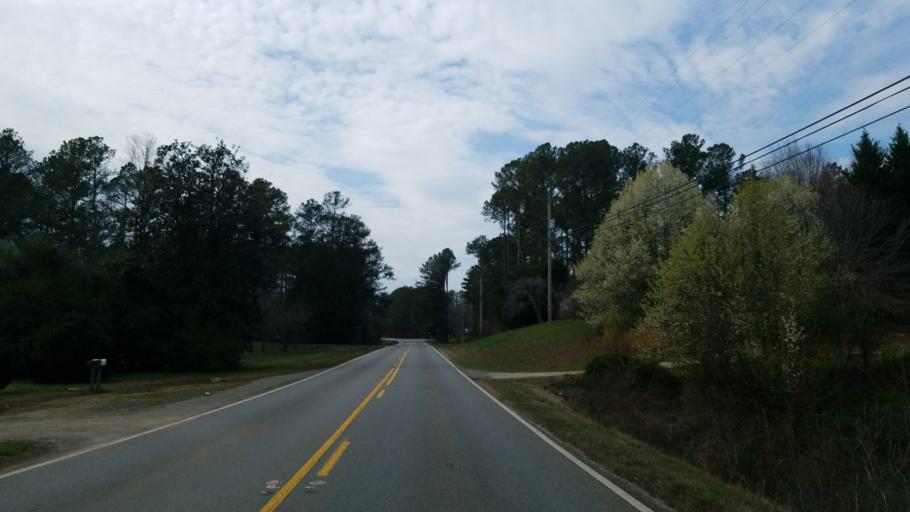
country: US
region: Georgia
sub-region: Cherokee County
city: Ball Ground
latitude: 34.3032
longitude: -84.3257
